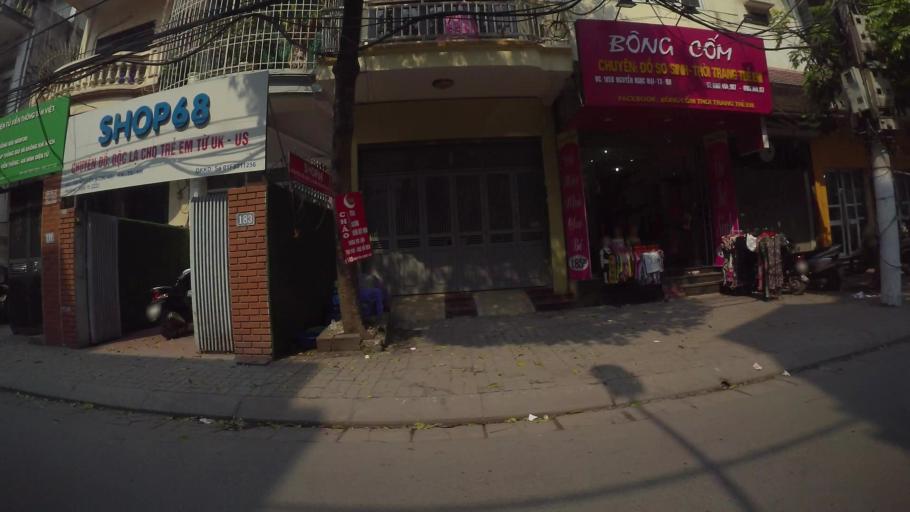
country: VN
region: Ha Noi
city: Dong Da
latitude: 20.9976
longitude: 105.8266
